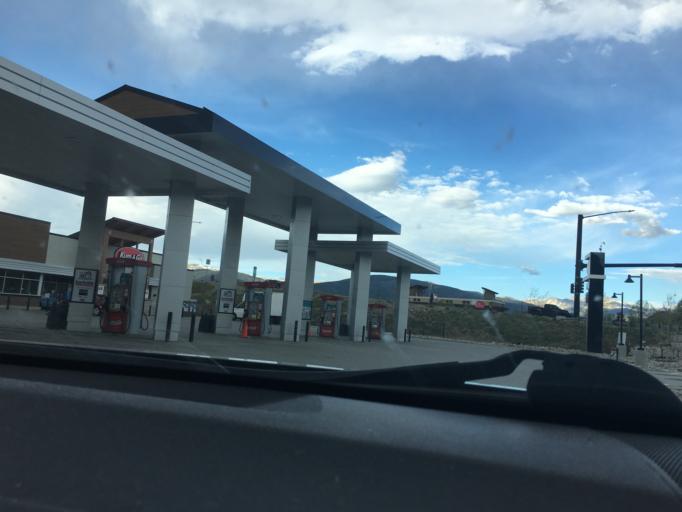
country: US
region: Colorado
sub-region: Summit County
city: Frisco
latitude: 39.5910
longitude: -106.0965
